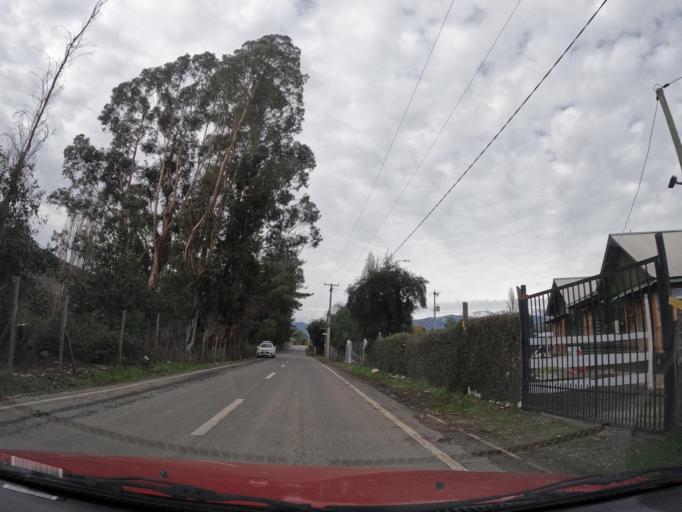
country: CL
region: Maule
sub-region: Provincia de Linares
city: Linares
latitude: -35.9229
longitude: -71.4057
